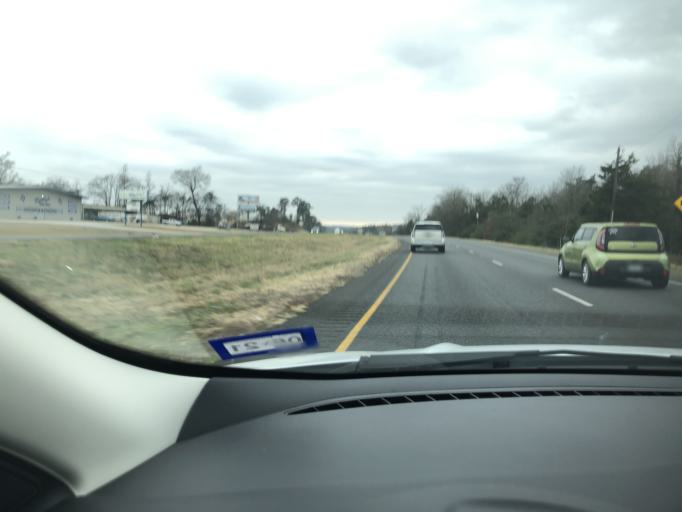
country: US
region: Texas
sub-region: Angelina County
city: Redland
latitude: 31.4910
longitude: -94.7178
